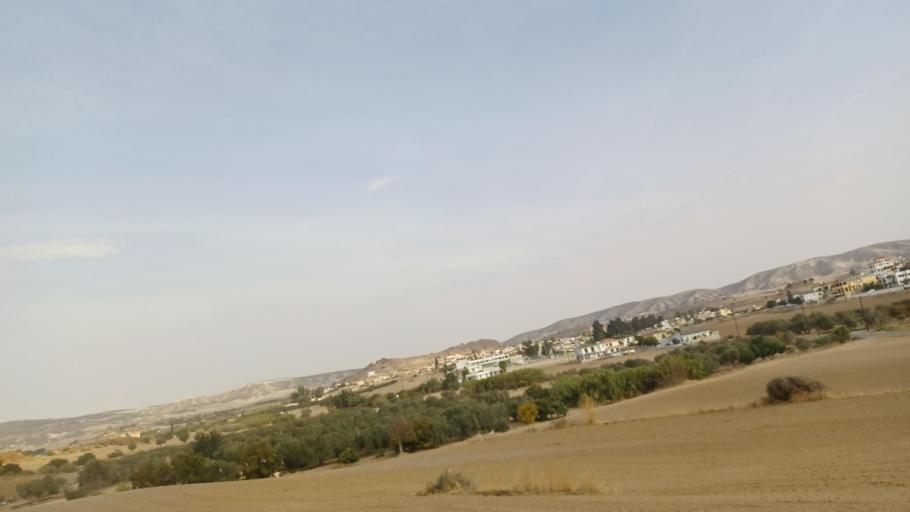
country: CY
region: Larnaka
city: Troulloi
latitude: 35.0243
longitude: 33.6104
